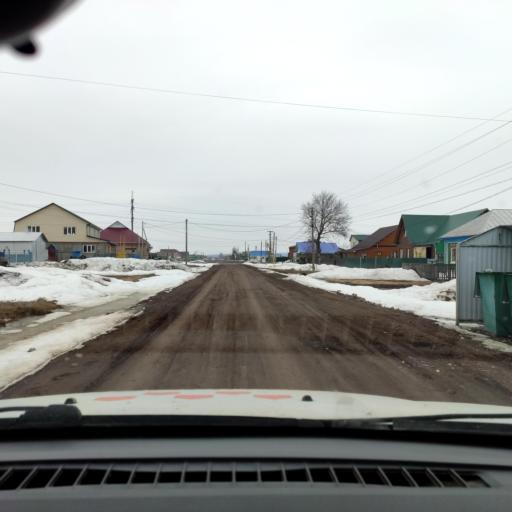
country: RU
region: Bashkortostan
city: Kushnarenkovo
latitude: 55.0771
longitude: 55.3881
